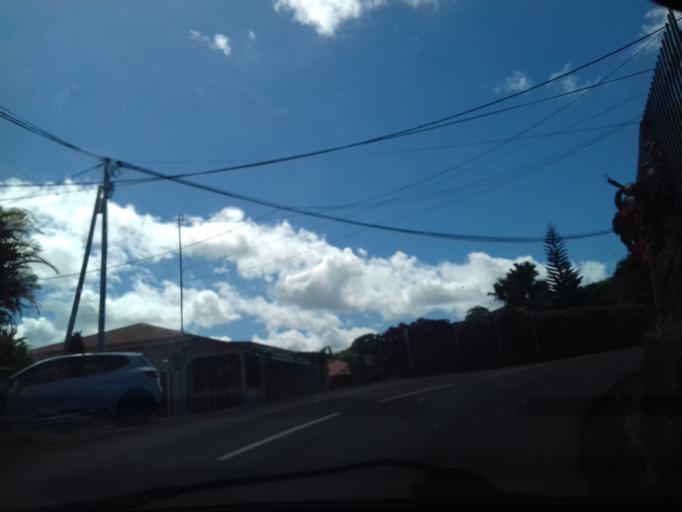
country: MQ
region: Martinique
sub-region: Martinique
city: Saint-Joseph
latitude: 14.6468
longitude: -61.0529
